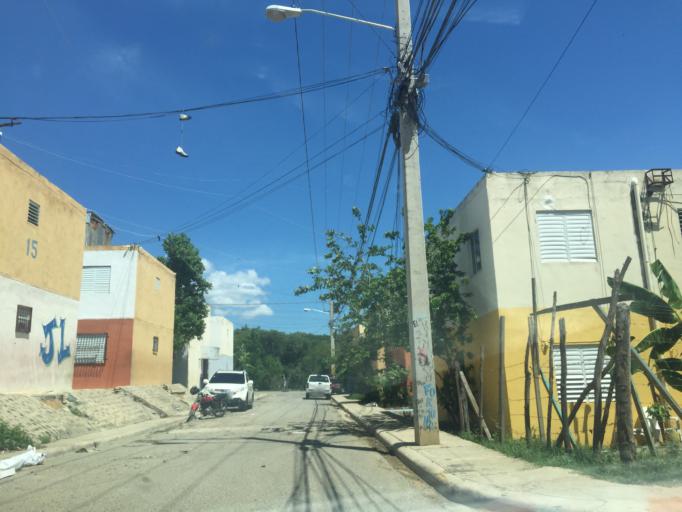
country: DO
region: Santiago
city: Santiago de los Caballeros
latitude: 19.4423
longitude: -70.7431
